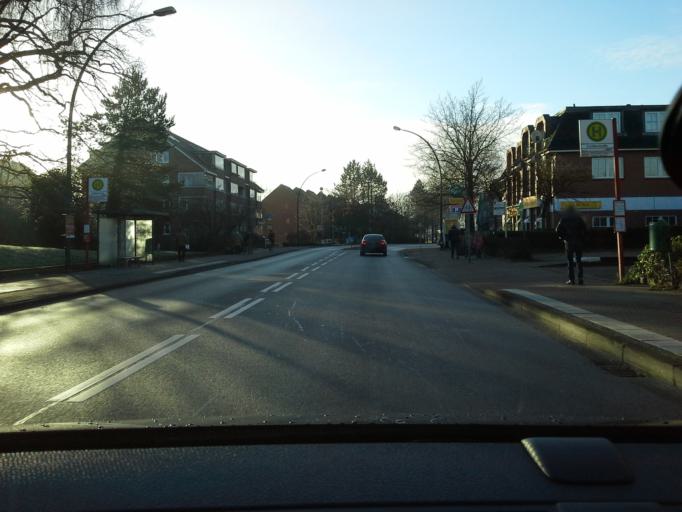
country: DE
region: Schleswig-Holstein
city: Pinneberg
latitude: 53.6668
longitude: 9.7938
